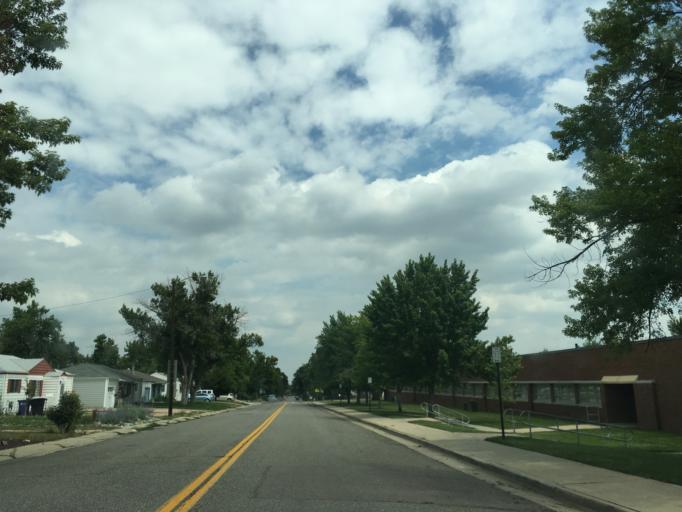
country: US
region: Colorado
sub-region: Arapahoe County
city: Sheridan
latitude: 39.6663
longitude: -105.0319
